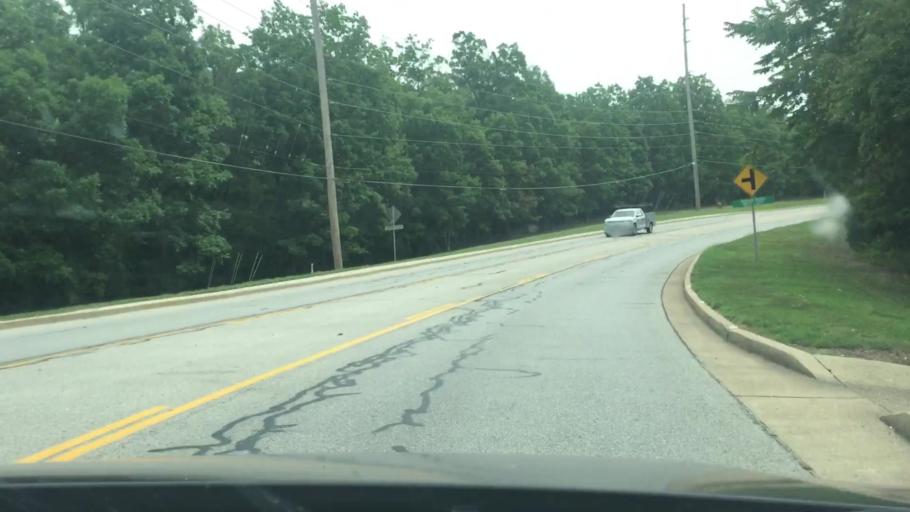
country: US
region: Missouri
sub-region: Camden County
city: Four Seasons
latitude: 38.1956
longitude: -92.6754
